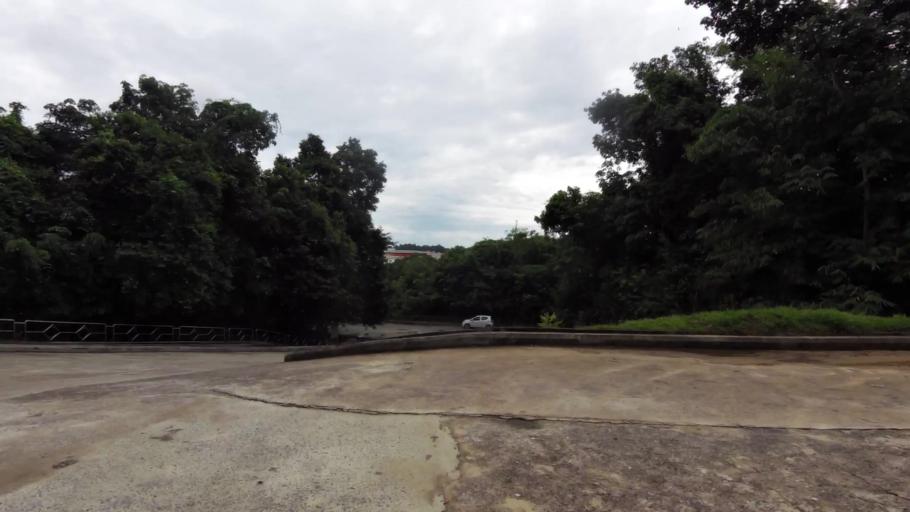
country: BN
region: Brunei and Muara
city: Bandar Seri Begawan
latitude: 4.8938
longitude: 114.9342
